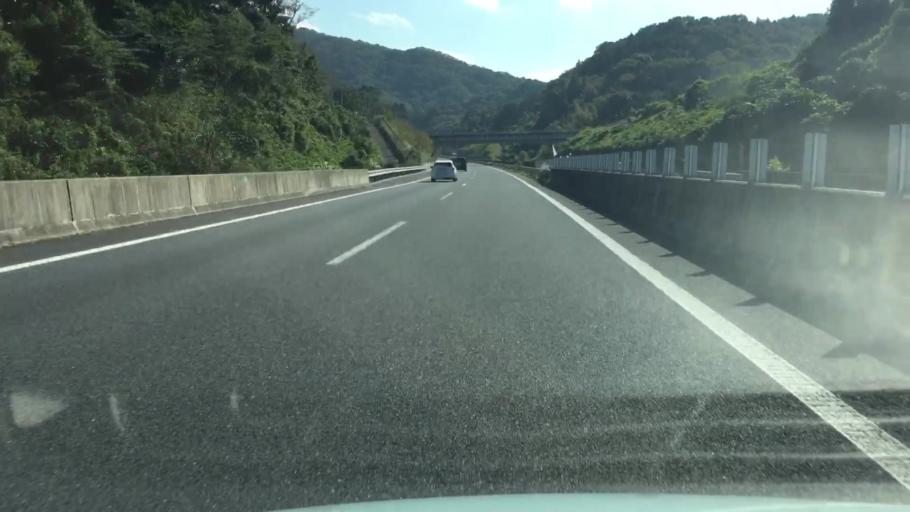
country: JP
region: Ibaraki
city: Kasama
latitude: 36.3409
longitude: 140.2232
